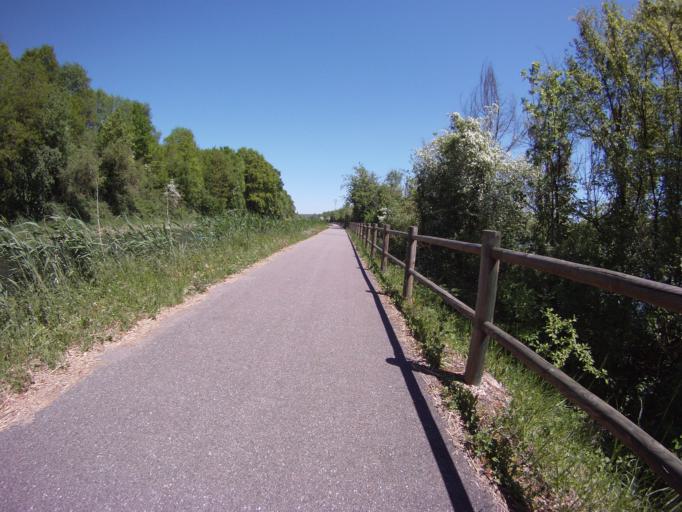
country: FR
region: Lorraine
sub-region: Departement de Meurthe-et-Moselle
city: Villey-Saint-Etienne
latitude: 48.7399
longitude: 5.9937
